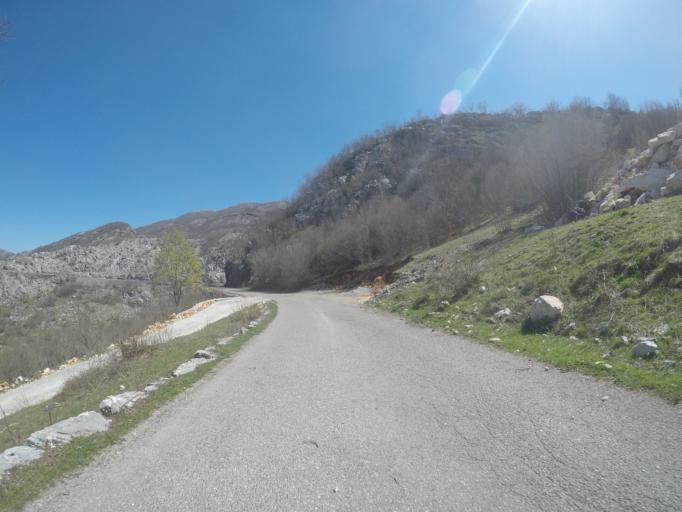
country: ME
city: Dobrota
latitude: 42.4694
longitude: 18.8571
